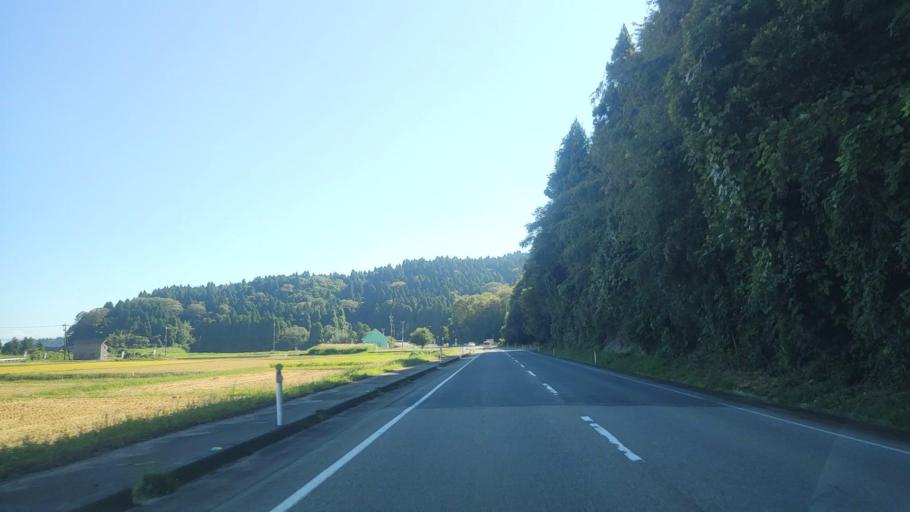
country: JP
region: Ishikawa
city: Nanao
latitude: 37.3890
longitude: 137.2333
